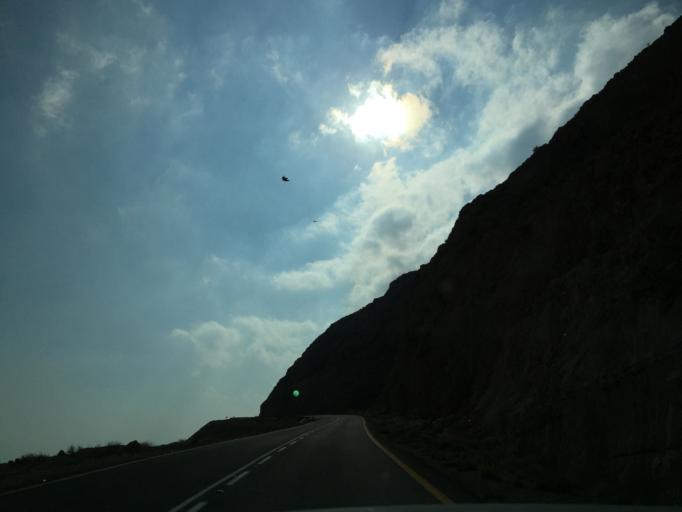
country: IL
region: Southern District
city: `En Boqeq
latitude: 31.3228
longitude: 35.3329
